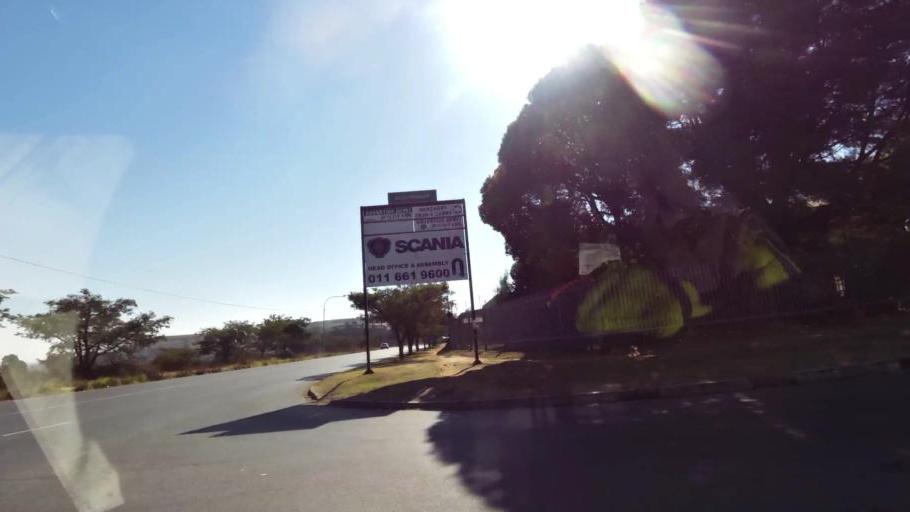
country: ZA
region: Gauteng
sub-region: City of Johannesburg Metropolitan Municipality
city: Johannesburg
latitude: -26.2538
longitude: 27.9733
